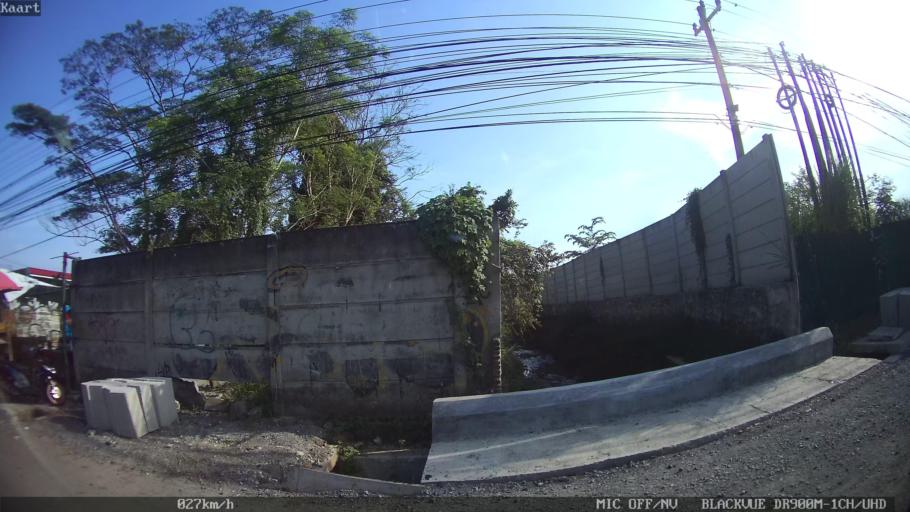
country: ID
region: Lampung
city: Kedaton
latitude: -5.3677
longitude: 105.2331
